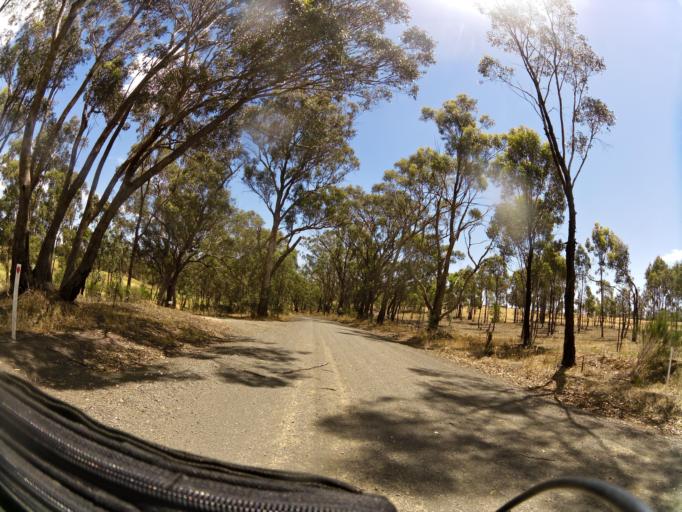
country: AU
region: Victoria
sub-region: Campaspe
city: Kyabram
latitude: -36.7947
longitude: 145.0839
